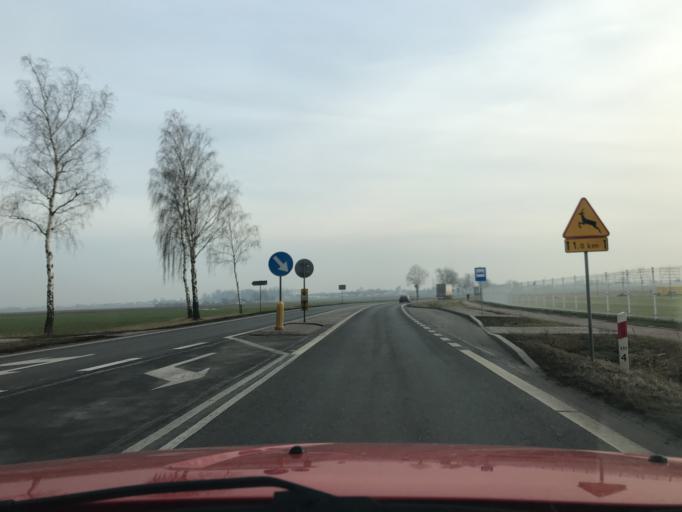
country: PL
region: Greater Poland Voivodeship
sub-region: Powiat pleszewski
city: Goluchow
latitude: 51.8207
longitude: 17.9746
